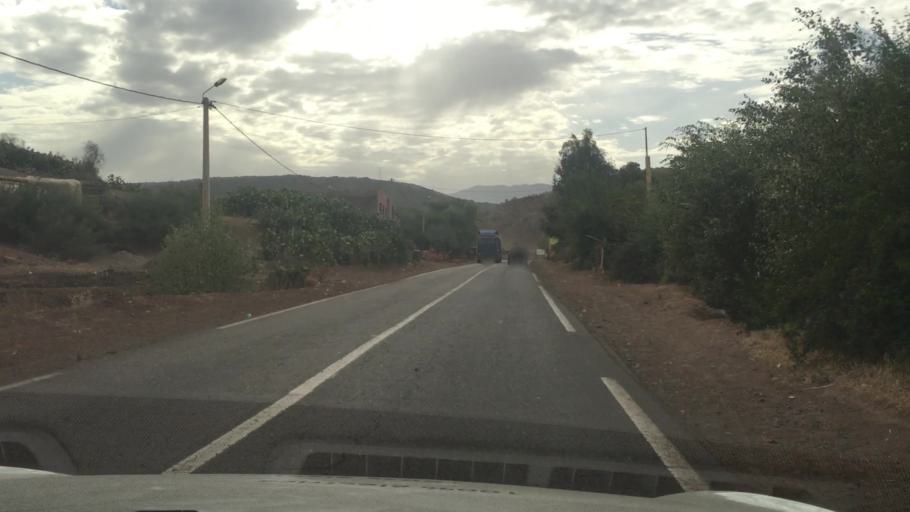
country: MA
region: Marrakech-Tensift-Al Haouz
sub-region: Al-Haouz
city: Touama
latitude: 31.5476
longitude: -7.5747
